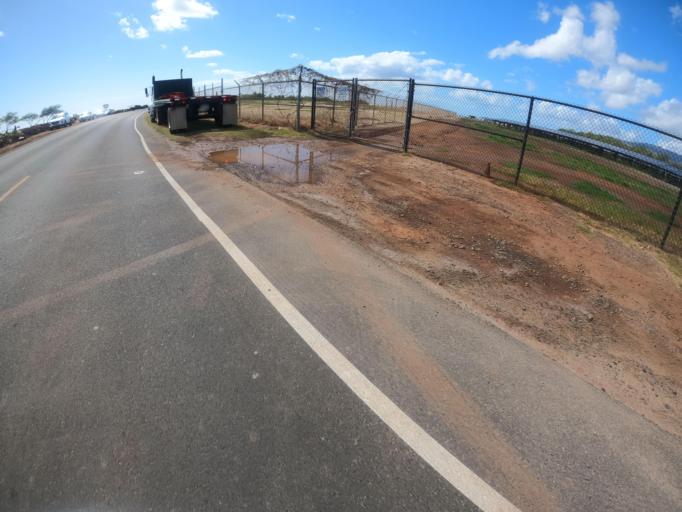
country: US
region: Hawaii
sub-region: Honolulu County
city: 'Ewa Villages
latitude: 21.3011
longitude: -158.0594
